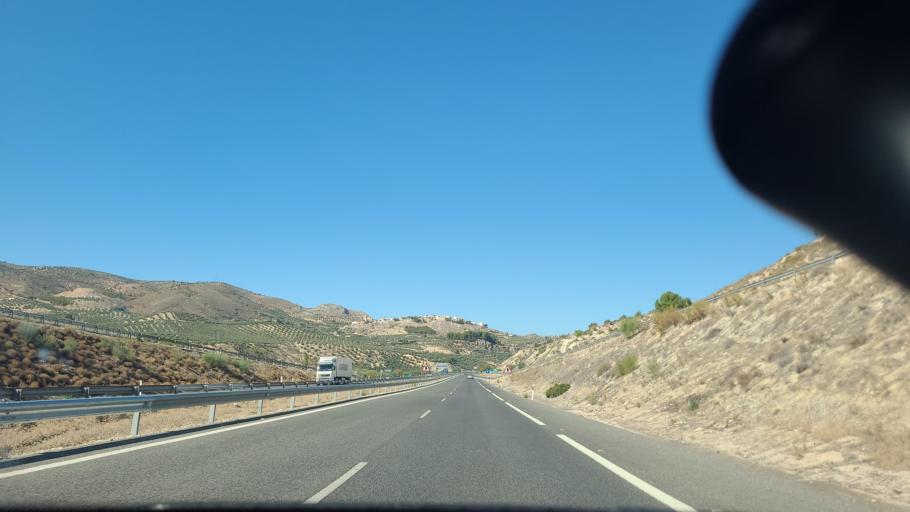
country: ES
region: Andalusia
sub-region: Provincia de Jaen
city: La Guardia de Jaen
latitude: 37.7258
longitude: -3.6797
